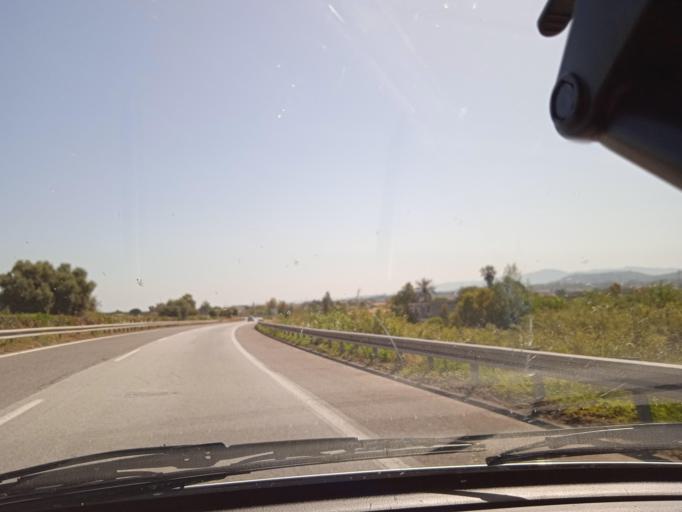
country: IT
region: Sicily
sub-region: Messina
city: Meri
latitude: 38.1753
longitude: 15.2396
